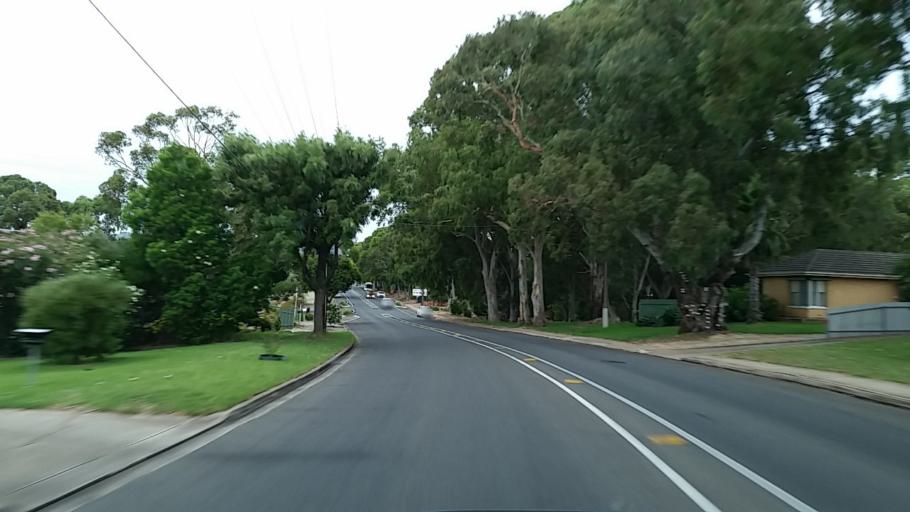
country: AU
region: South Australia
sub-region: Campbelltown
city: Athelstone
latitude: -34.8684
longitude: 138.6899
